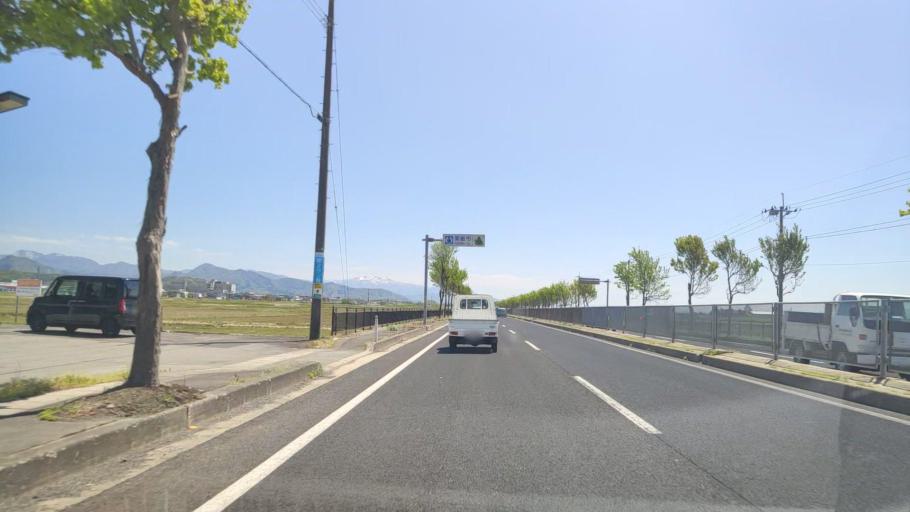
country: JP
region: Yamagata
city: Higashine
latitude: 38.4721
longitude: 140.3828
